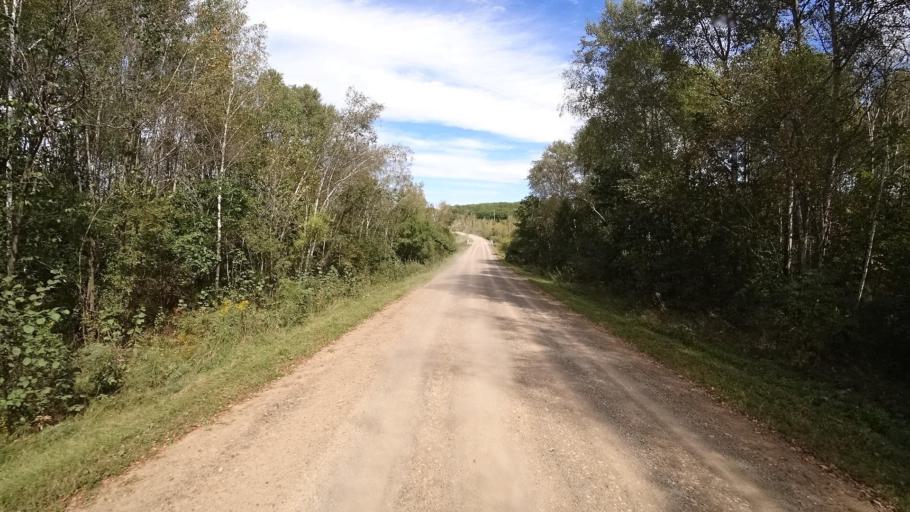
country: RU
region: Primorskiy
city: Yakovlevka
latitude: 44.6781
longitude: 133.6141
